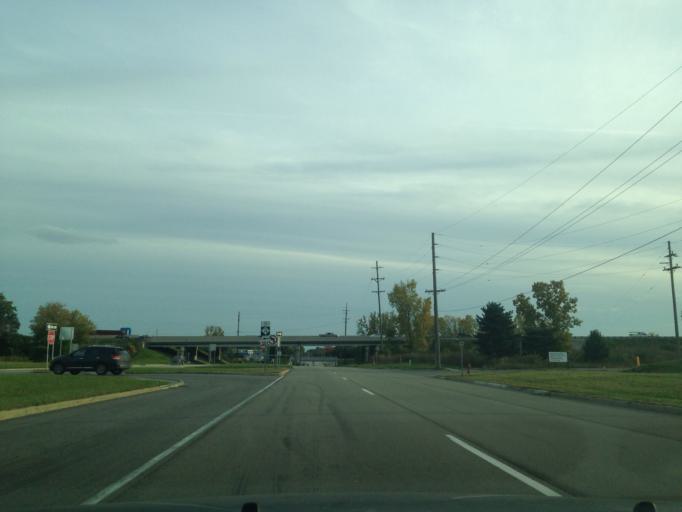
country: US
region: Michigan
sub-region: Wayne County
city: Plymouth
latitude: 42.3853
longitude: -83.4810
